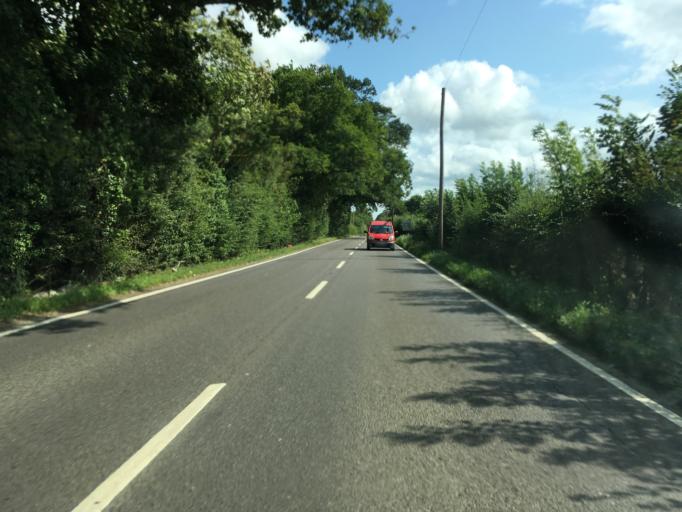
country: GB
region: England
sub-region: Kent
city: Headcorn
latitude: 51.1920
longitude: 0.6023
